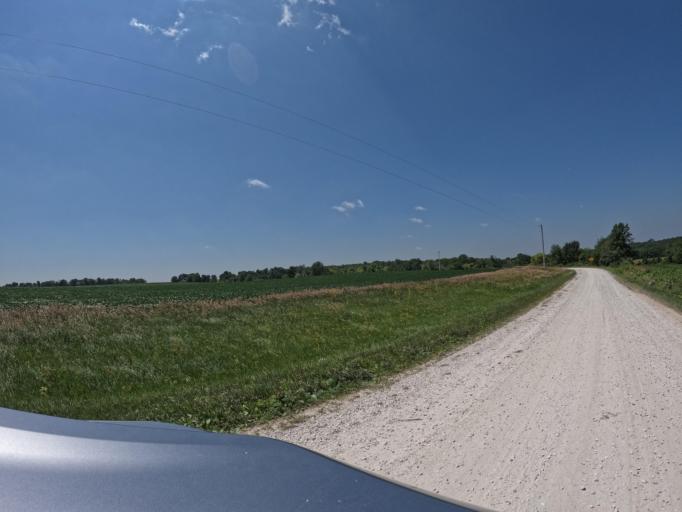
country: US
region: Iowa
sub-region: Keokuk County
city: Sigourney
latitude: 41.2886
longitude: -92.2368
